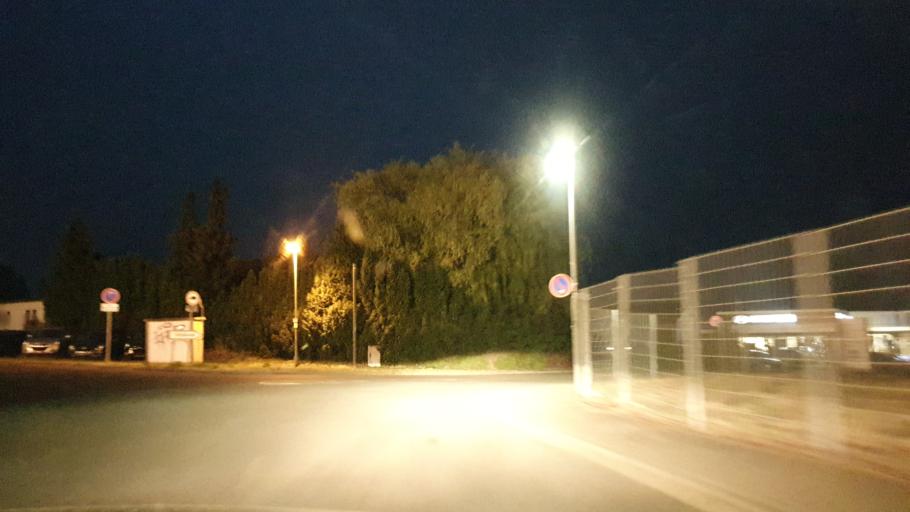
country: DE
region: Rheinland-Pfalz
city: Andernach
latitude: 50.4131
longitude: 7.4074
